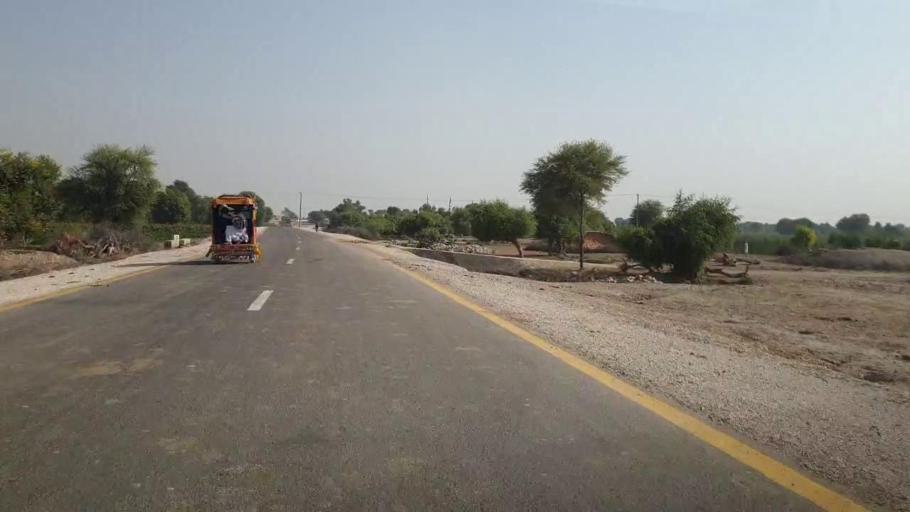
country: PK
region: Sindh
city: Bhan
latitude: 26.5654
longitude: 67.7702
